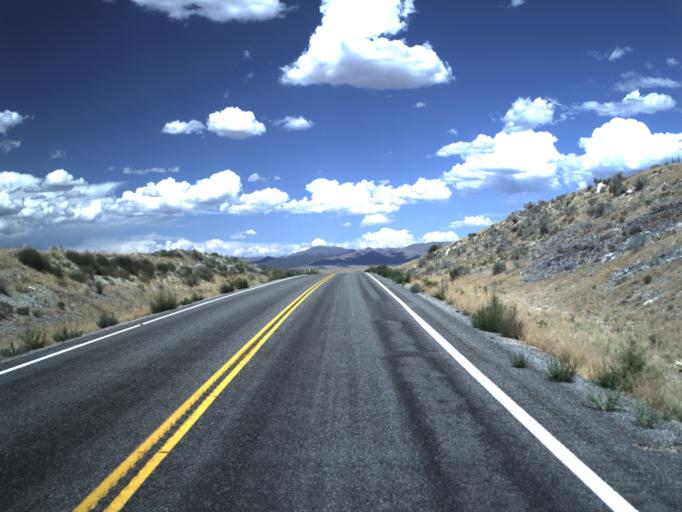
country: US
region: Utah
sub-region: Millard County
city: Delta
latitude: 39.6473
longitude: -112.2995
